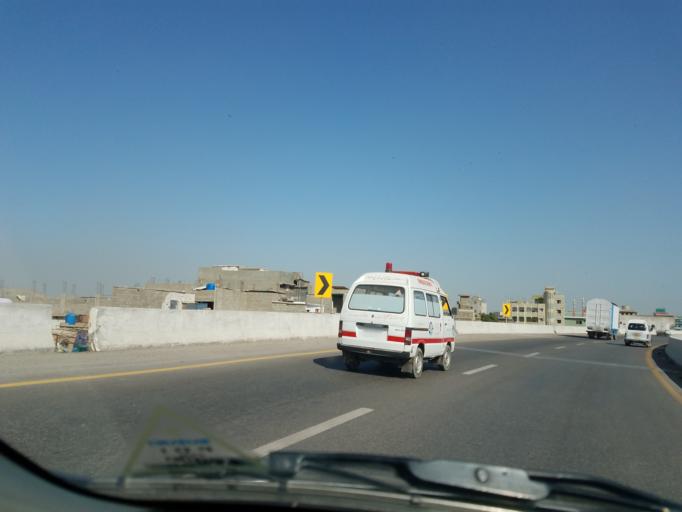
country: PK
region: Sindh
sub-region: Karachi District
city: Karachi
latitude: 24.8825
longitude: 67.0043
